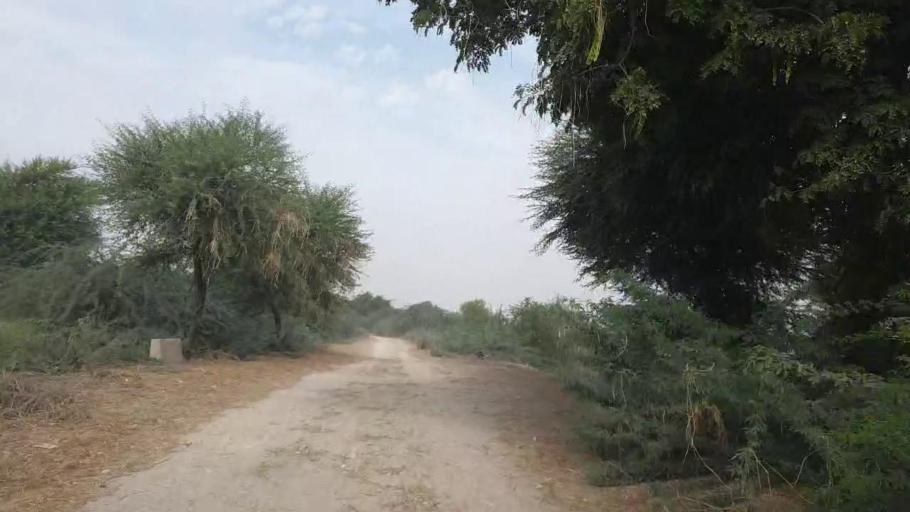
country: PK
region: Sindh
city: Rajo Khanani
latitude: 24.9467
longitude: 68.9800
